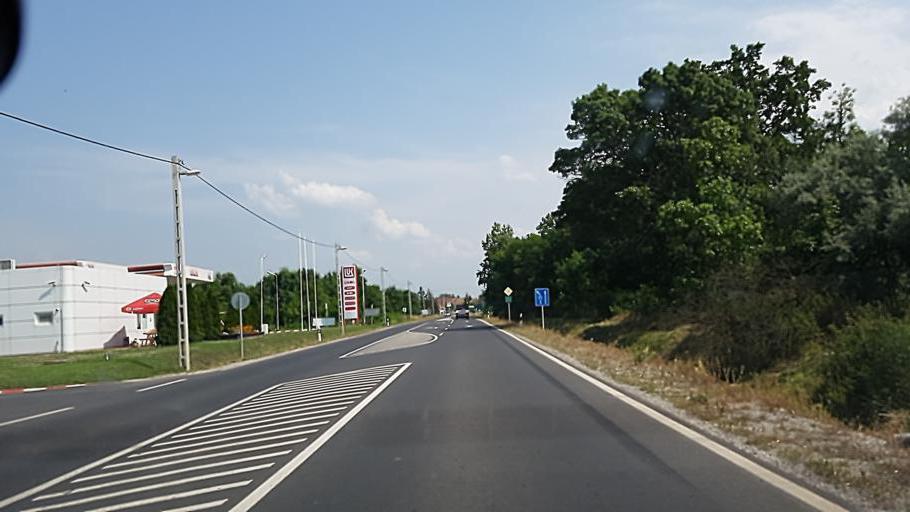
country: HU
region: Heves
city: Poroszlo
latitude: 47.6447
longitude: 20.6356
